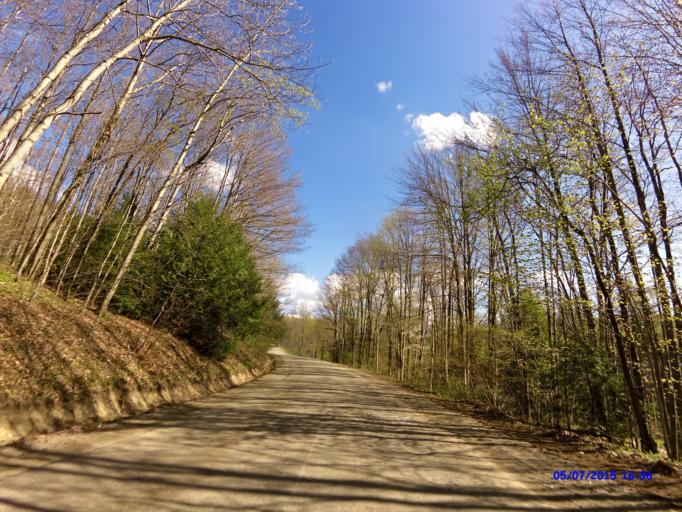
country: US
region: New York
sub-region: Cattaraugus County
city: Little Valley
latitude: 42.3204
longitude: -78.6908
